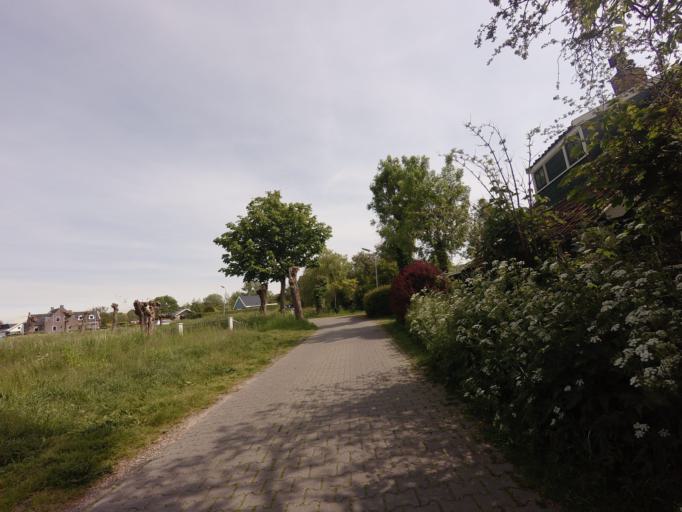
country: NL
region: North Holland
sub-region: Gemeente Uitgeest
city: Uitgeest
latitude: 52.5143
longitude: 4.7707
